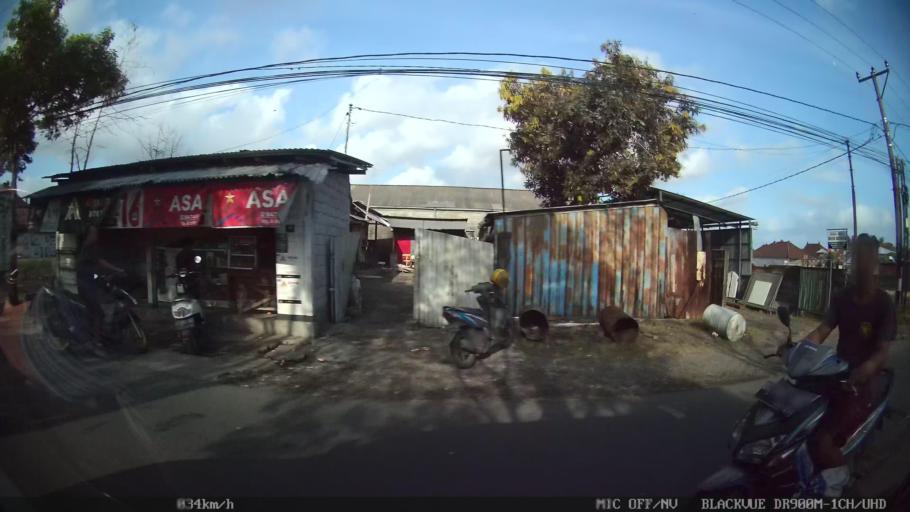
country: ID
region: Bali
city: Banjar Sedang
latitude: -8.5672
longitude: 115.2345
